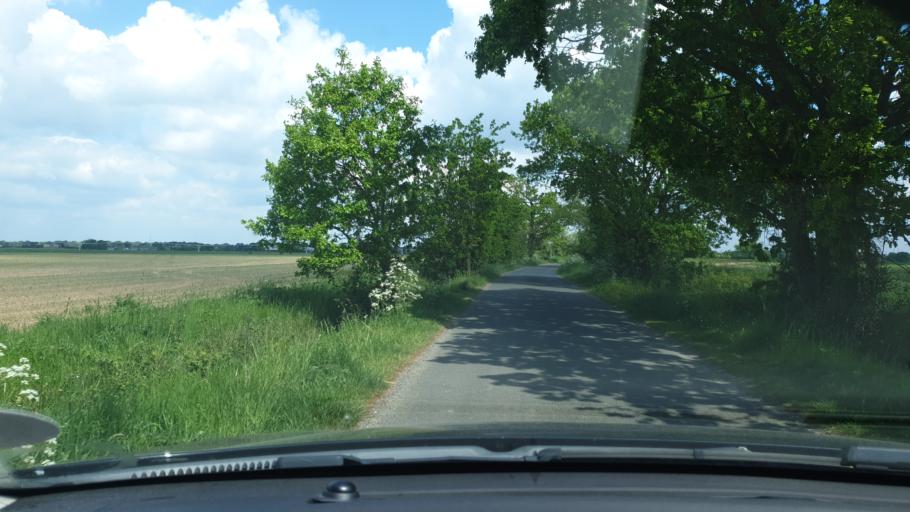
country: GB
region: England
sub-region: Essex
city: Great Bentley
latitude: 51.8437
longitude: 1.0744
